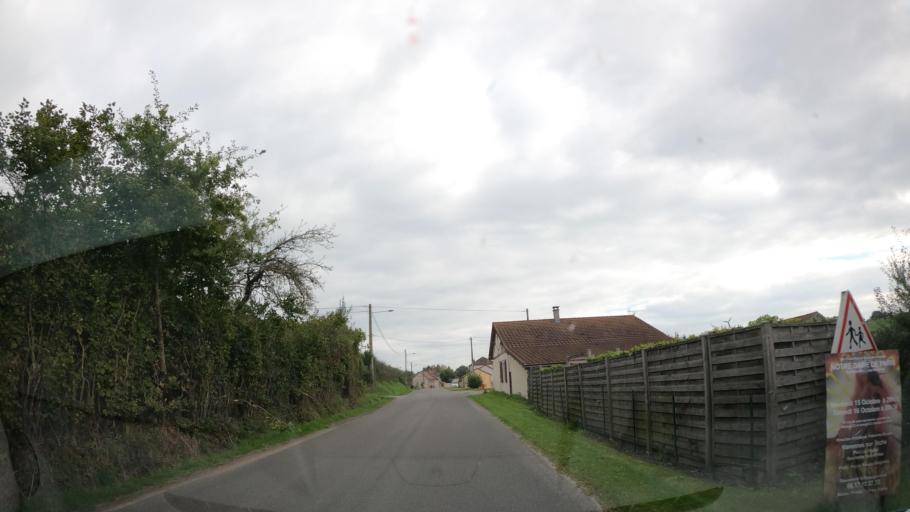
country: FR
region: Auvergne
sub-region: Departement de l'Allier
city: Lapalisse
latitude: 46.3271
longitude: 3.6261
